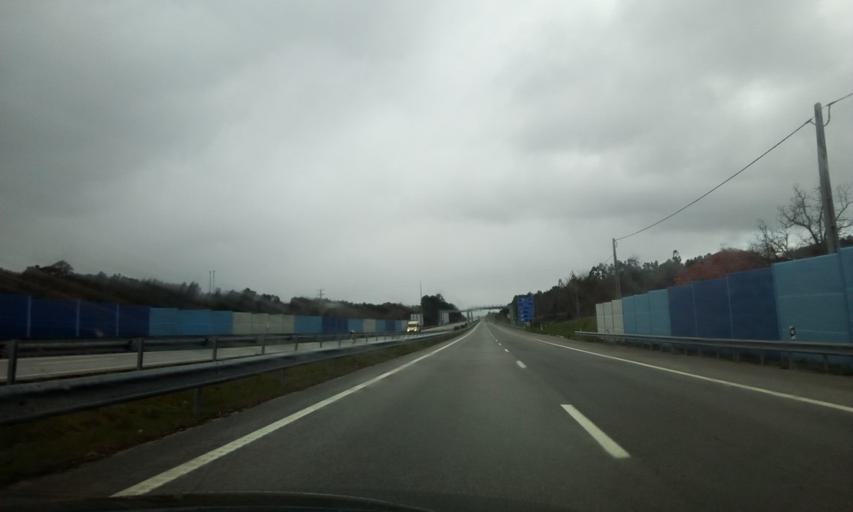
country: PT
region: Guarda
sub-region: Fornos de Algodres
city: Fornos de Algodres
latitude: 40.6132
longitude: -7.6466
